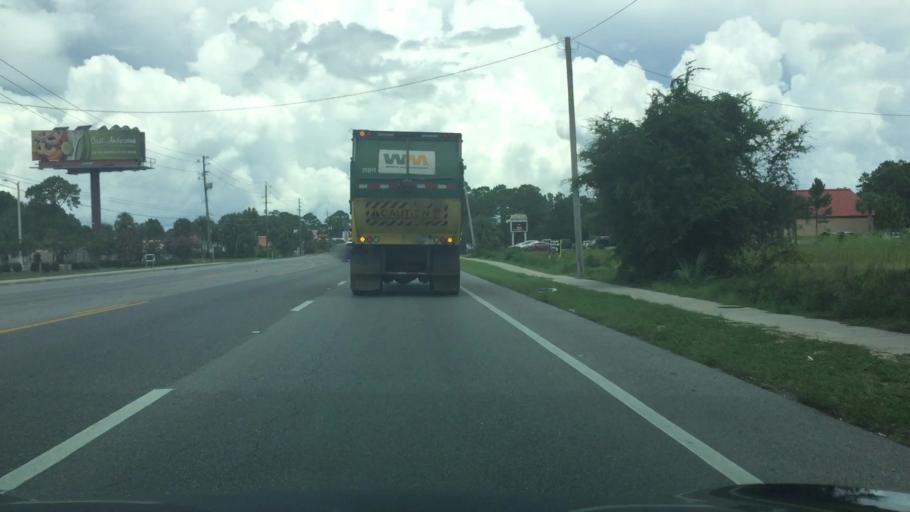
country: US
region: Florida
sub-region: Bay County
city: Lower Grand Lagoon
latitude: 30.1550
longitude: -85.7513
